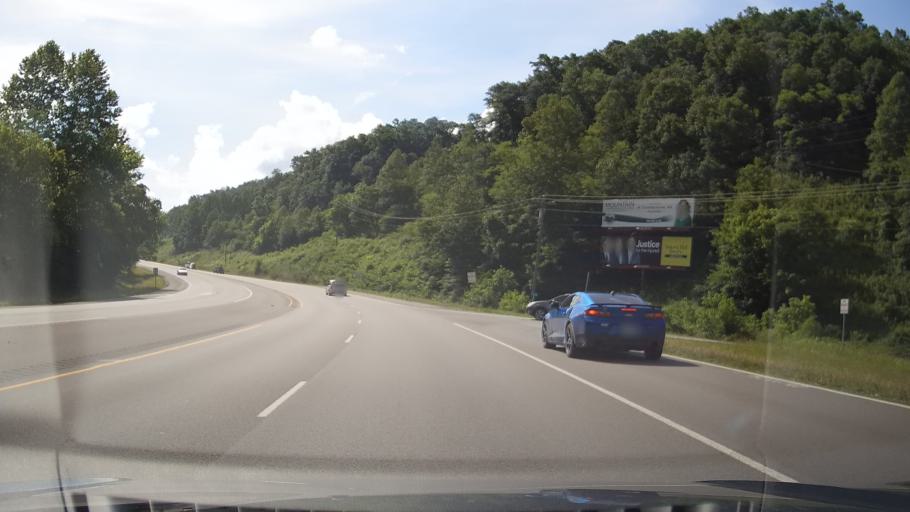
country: US
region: Kentucky
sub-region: Floyd County
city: Prestonsburg
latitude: 37.6415
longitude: -82.7579
